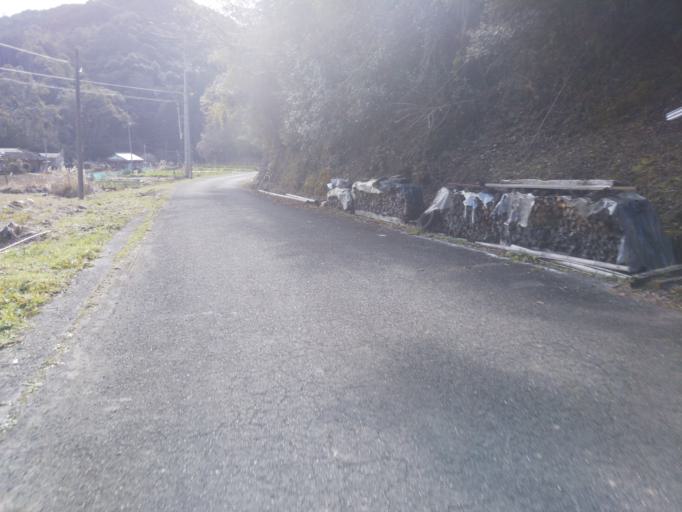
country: JP
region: Kochi
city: Nakamura
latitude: 33.0457
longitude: 132.9874
